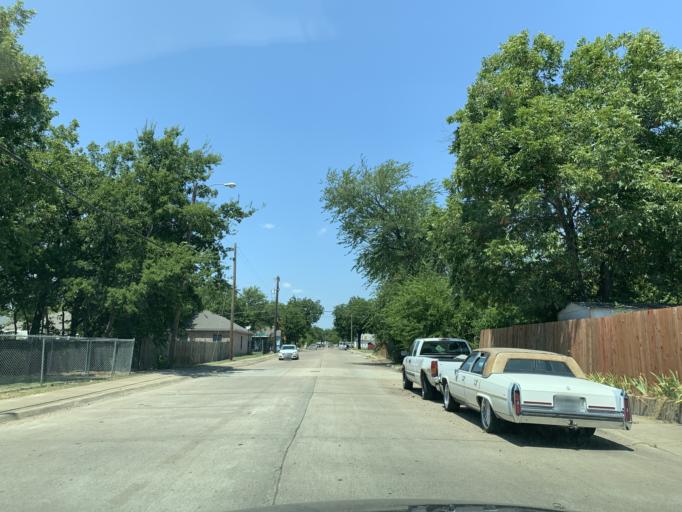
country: US
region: Texas
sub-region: Dallas County
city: Dallas
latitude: 32.6916
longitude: -96.8013
